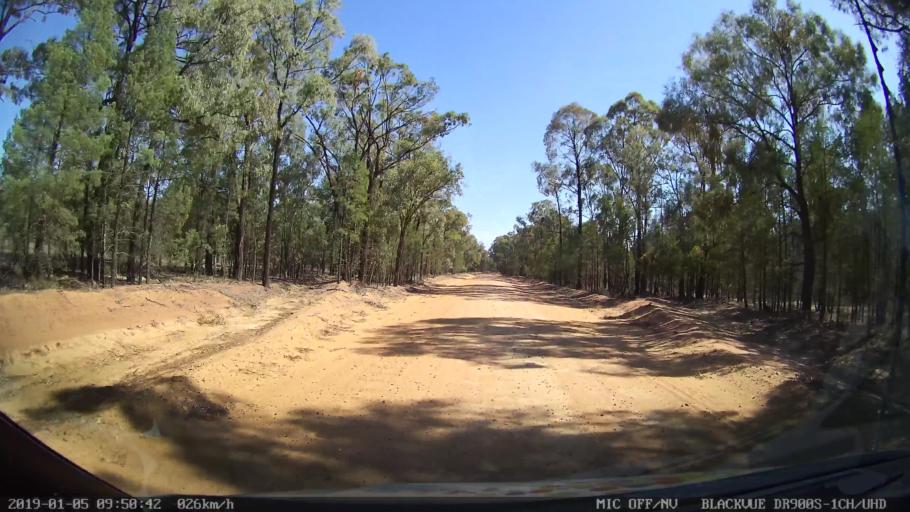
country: AU
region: New South Wales
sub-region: Gilgandra
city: Gilgandra
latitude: -31.6636
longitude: 148.7590
